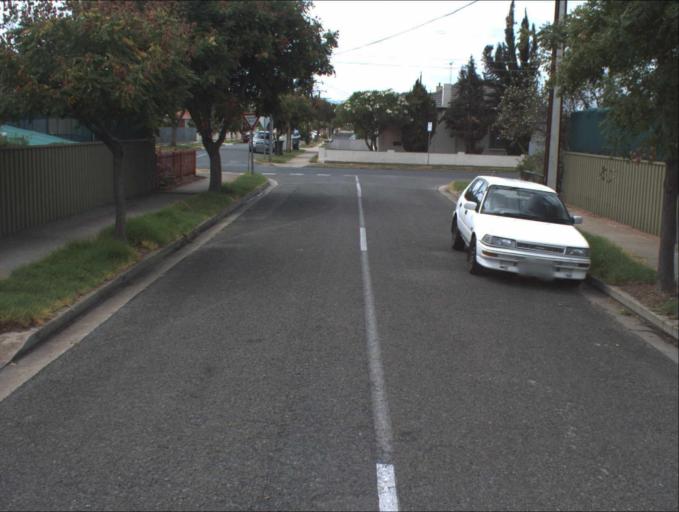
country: AU
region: South Australia
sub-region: Charles Sturt
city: Woodville
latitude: -34.8818
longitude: 138.5611
